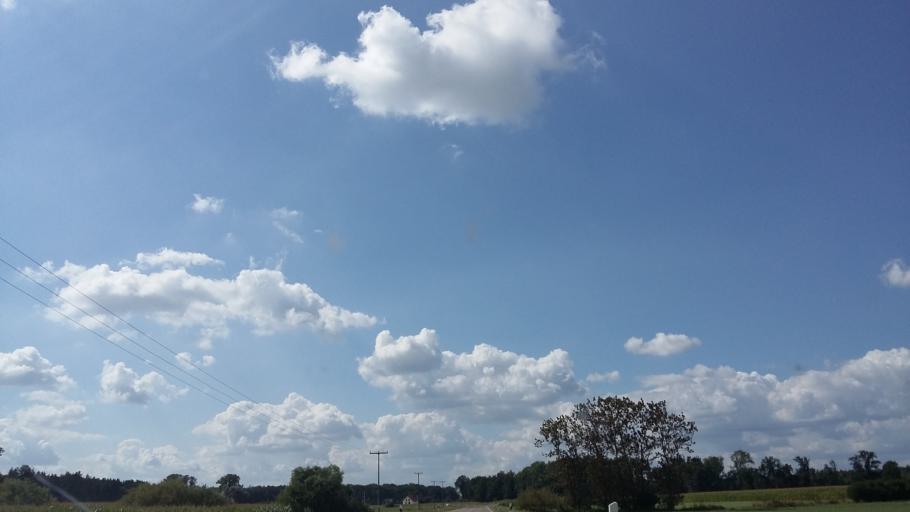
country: DE
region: Bavaria
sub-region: Swabia
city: Pfaffenhofen an der Roth
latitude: 48.3519
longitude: 10.1309
